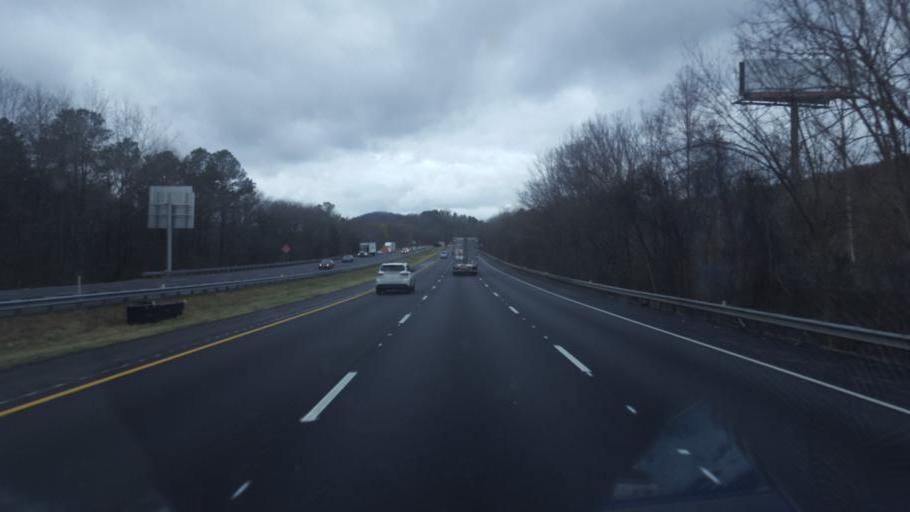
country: US
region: Georgia
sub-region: Whitfield County
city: Dalton
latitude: 34.8016
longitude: -85.0092
